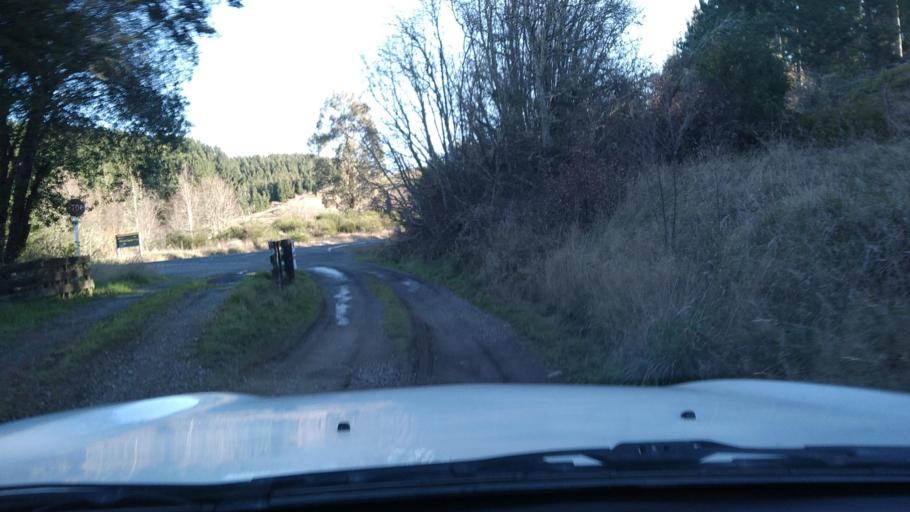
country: NZ
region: Waikato
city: Turangi
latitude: -38.6531
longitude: 175.7046
